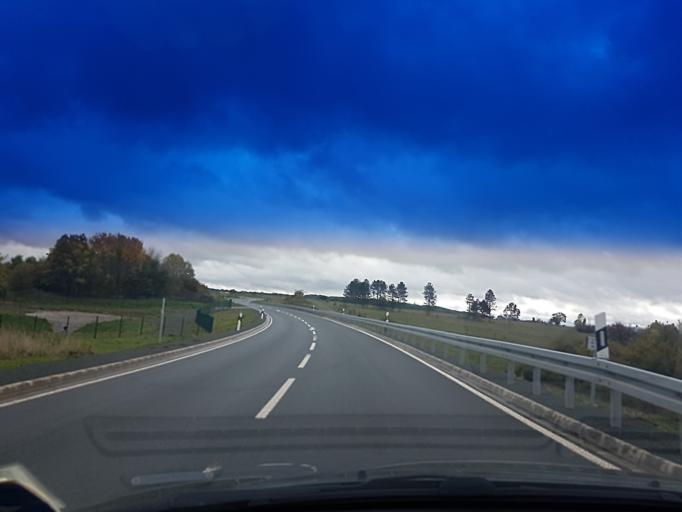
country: DE
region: Bavaria
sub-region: Upper Franconia
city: Bindlach
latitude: 49.9929
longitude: 11.6233
